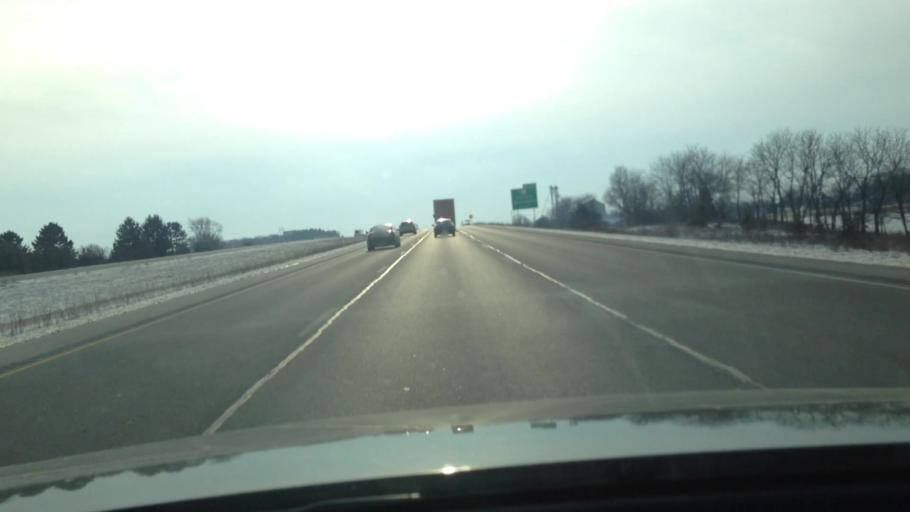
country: US
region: Wisconsin
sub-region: Walworth County
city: Elkhorn
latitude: 42.7091
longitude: -88.4817
